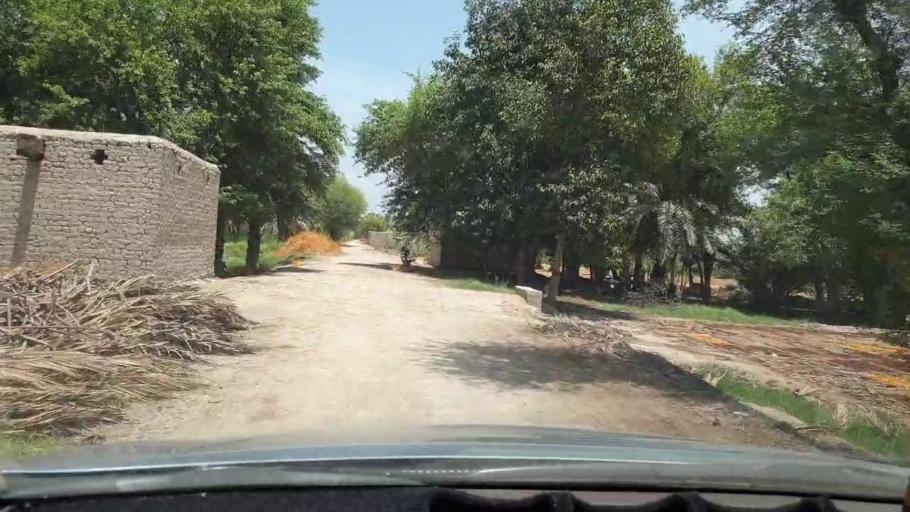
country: PK
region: Sindh
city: Khairpur
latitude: 27.4478
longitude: 68.7784
